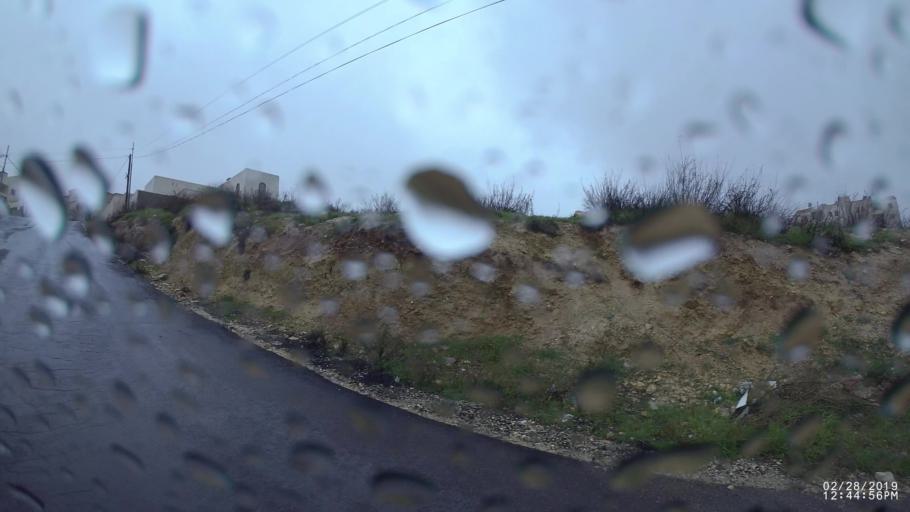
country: JO
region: Amman
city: Al Jubayhah
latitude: 32.0278
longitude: 35.8831
